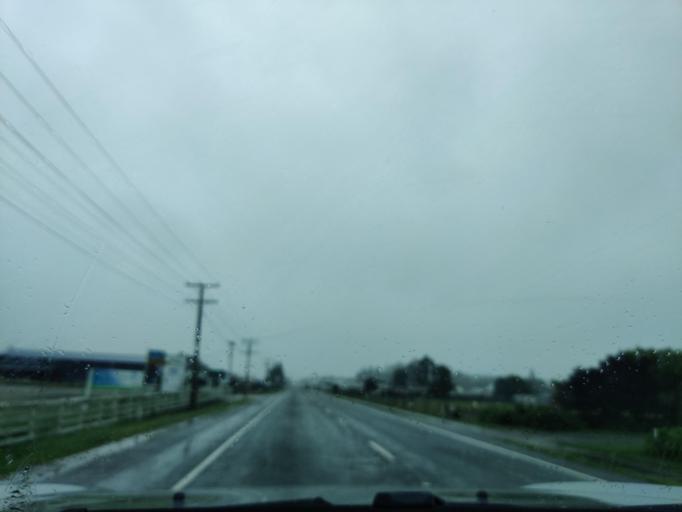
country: NZ
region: Hawke's Bay
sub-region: Hastings District
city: Hastings
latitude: -39.9926
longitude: 176.5405
